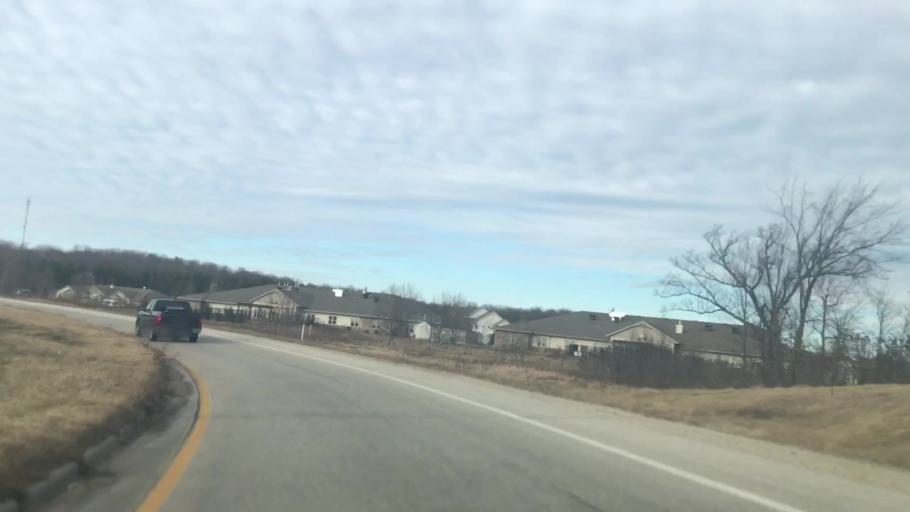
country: US
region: Wisconsin
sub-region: Washington County
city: Slinger
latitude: 43.3260
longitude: -88.2492
